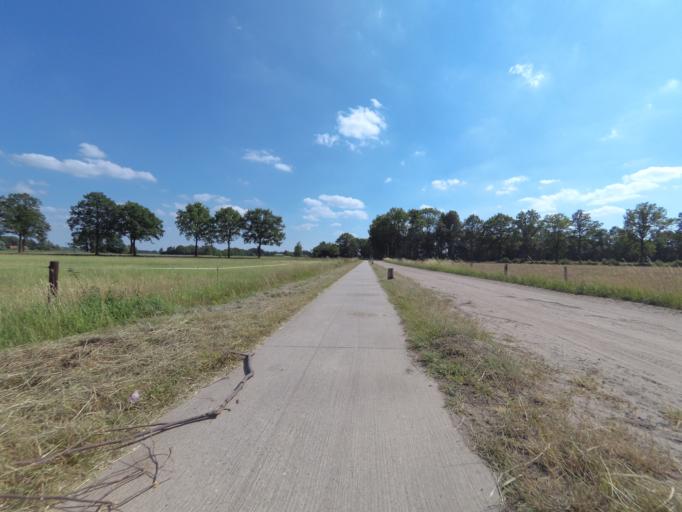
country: NL
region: Overijssel
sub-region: Gemeente Oldenzaal
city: Oldenzaal
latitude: 52.3607
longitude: 6.9041
